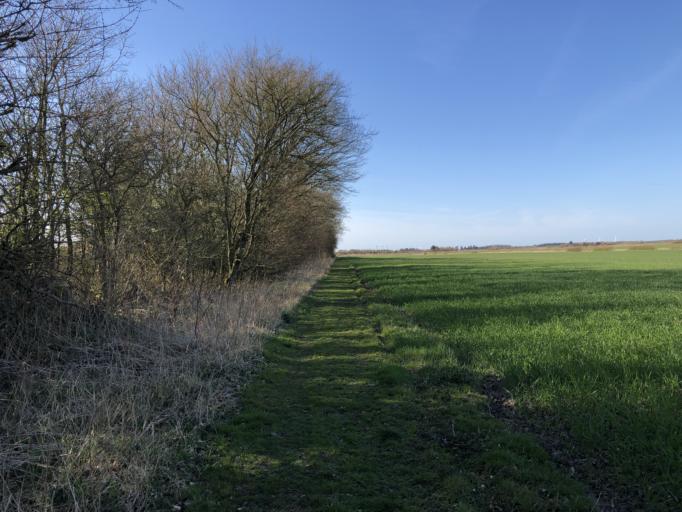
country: DK
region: Central Jutland
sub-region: Holstebro Kommune
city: Ulfborg
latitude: 56.3256
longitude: 8.3200
